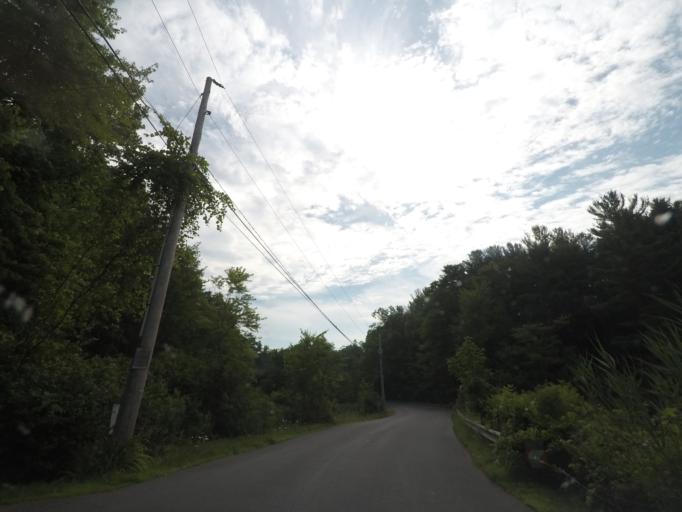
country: US
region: New York
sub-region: Rensselaer County
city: Averill Park
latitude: 42.6431
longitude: -73.5519
